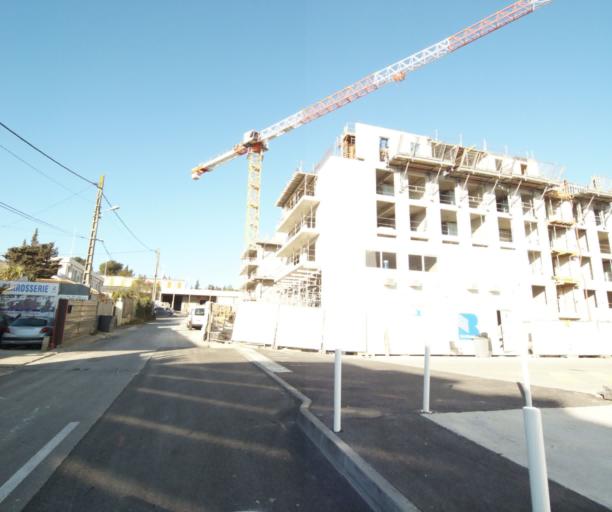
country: FR
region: Provence-Alpes-Cote d'Azur
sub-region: Departement des Alpes-Maritimes
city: Biot
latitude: 43.5995
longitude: 7.0847
